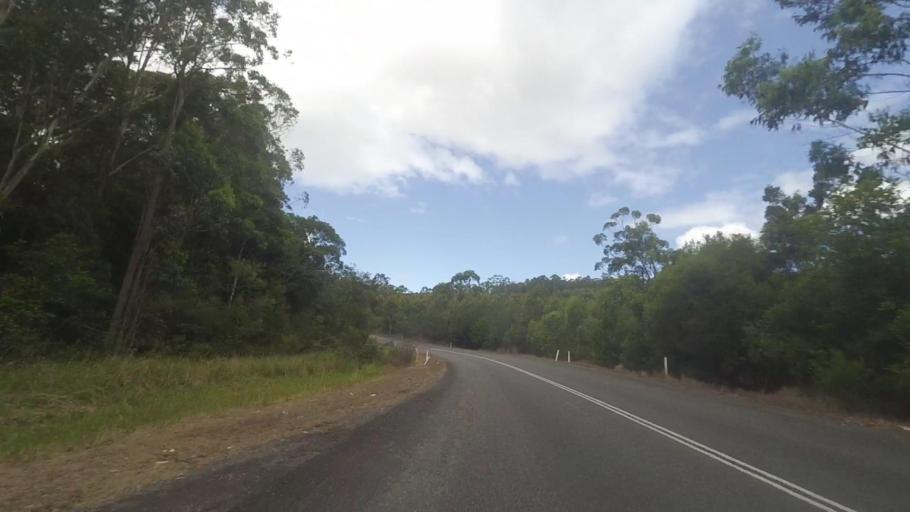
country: AU
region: New South Wales
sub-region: Great Lakes
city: Bulahdelah
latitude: -32.3883
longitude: 152.2398
